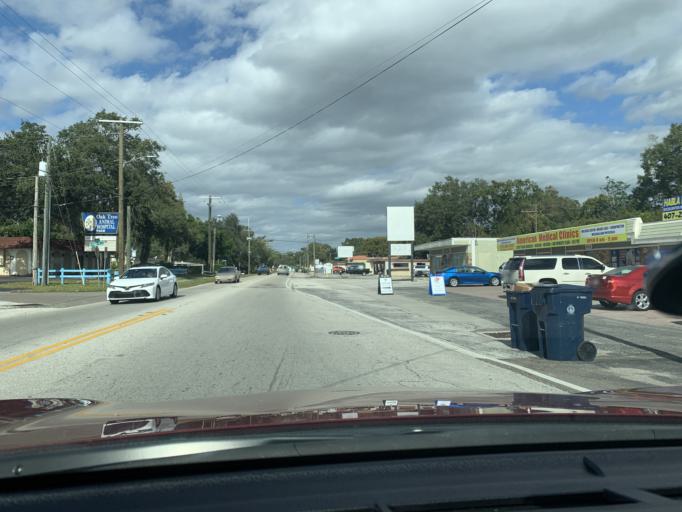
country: US
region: Florida
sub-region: Hillsborough County
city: Egypt Lake-Leto
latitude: 28.0122
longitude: -82.4847
